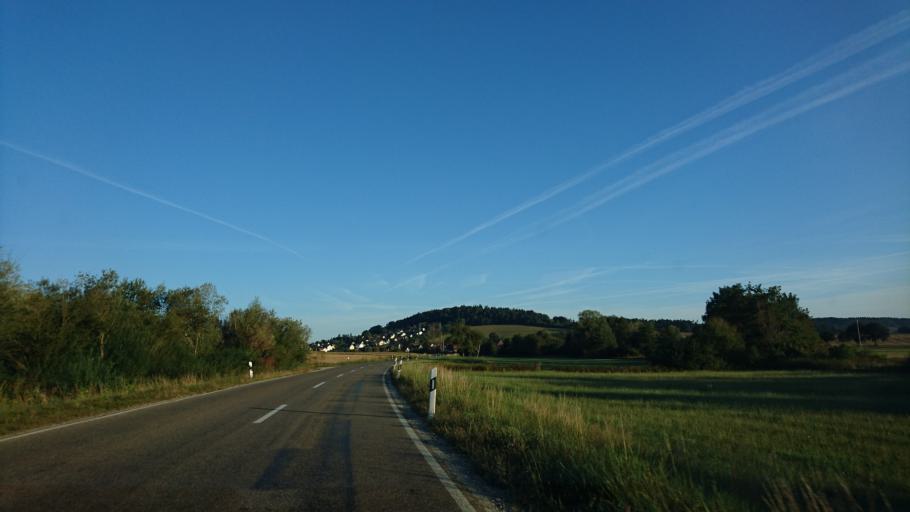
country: DE
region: Bavaria
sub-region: Regierungsbezirk Mittelfranken
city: Thalmassing
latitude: 49.0835
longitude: 11.2416
